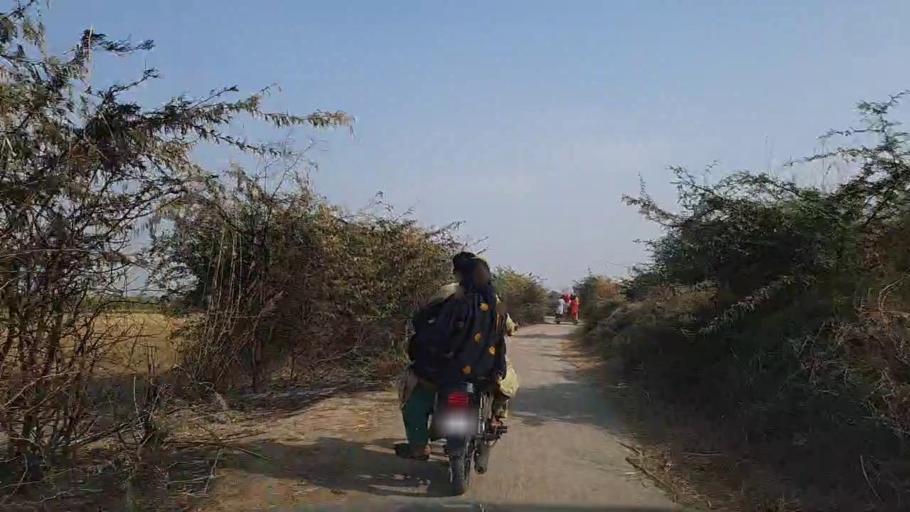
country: PK
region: Sindh
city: Thatta
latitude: 24.6485
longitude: 67.9262
